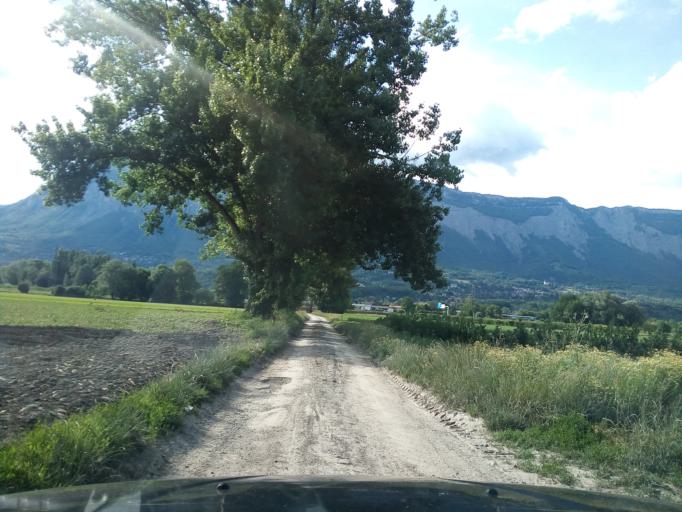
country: FR
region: Rhone-Alpes
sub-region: Departement de l'Isere
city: Montbonnot-Saint-Martin
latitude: 45.2140
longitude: 5.8188
